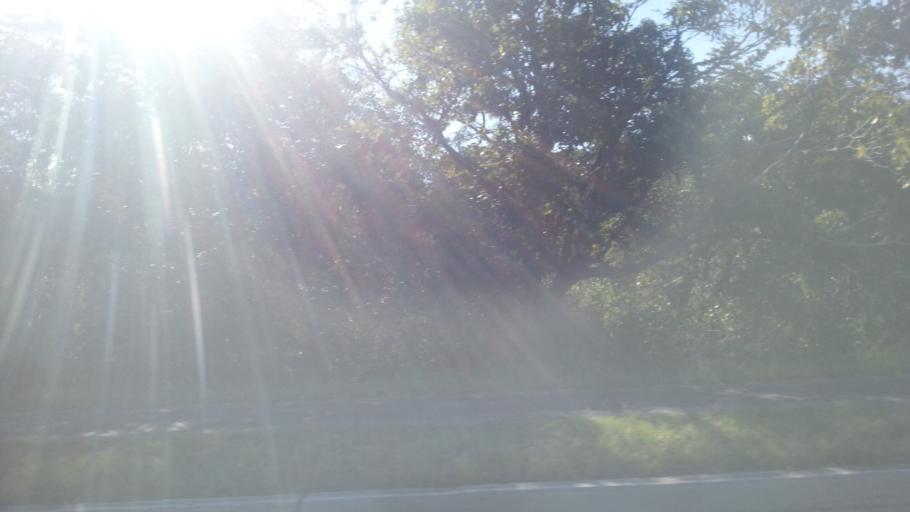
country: AU
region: New South Wales
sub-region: Wollongong
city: Berkeley
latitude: -34.4671
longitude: 150.8530
